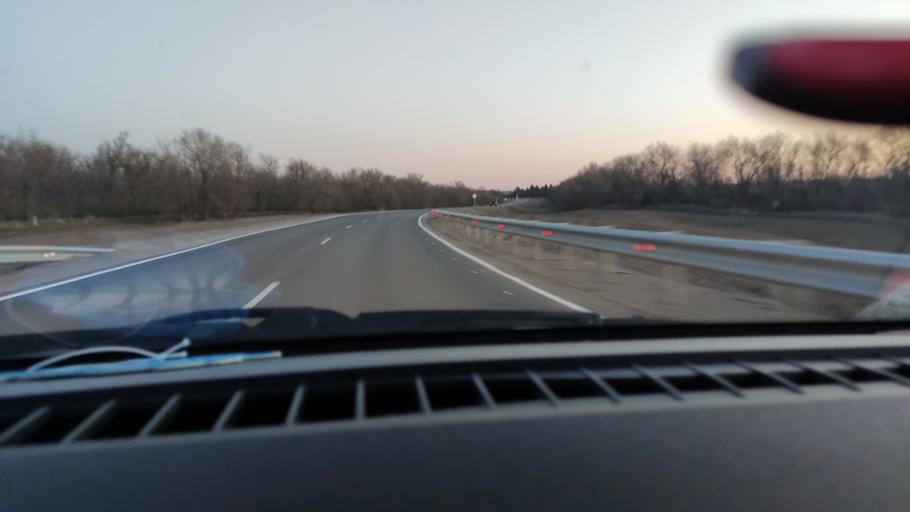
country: RU
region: Saratov
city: Krasnoarmeysk
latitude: 51.1029
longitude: 45.9538
